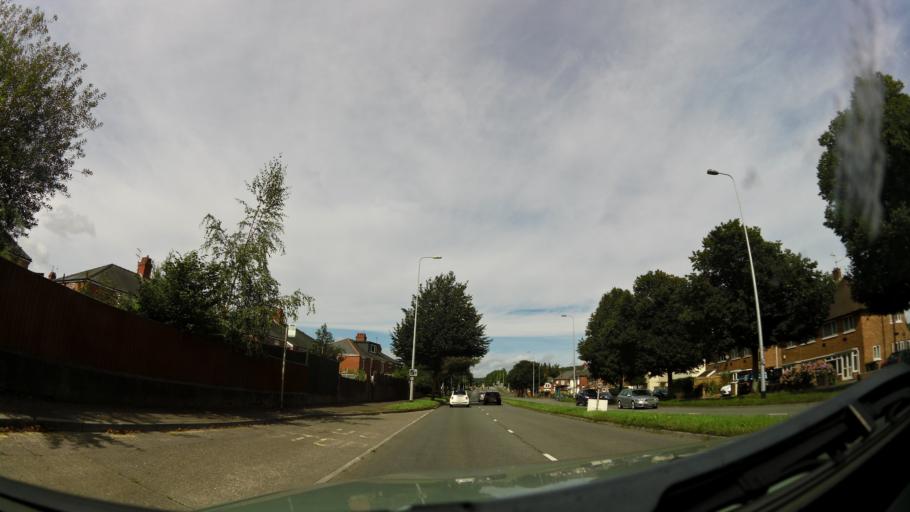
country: GB
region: Wales
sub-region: Cardiff
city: Radyr
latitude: 51.5186
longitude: -3.2203
